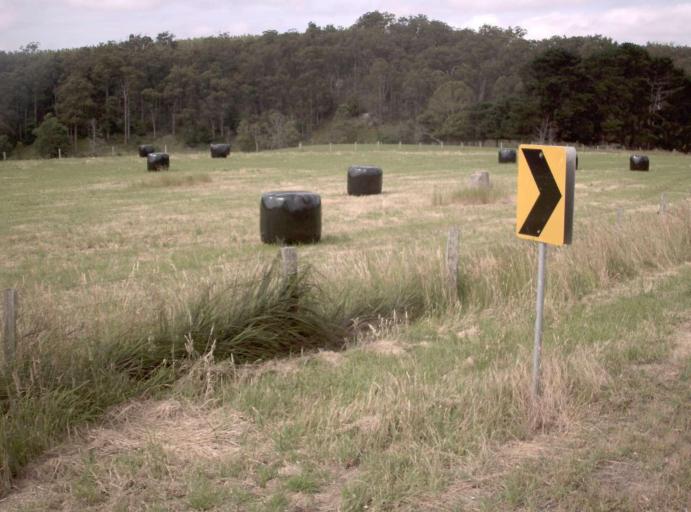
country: AU
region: Victoria
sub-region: Latrobe
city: Traralgon
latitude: -38.3790
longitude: 146.7901
